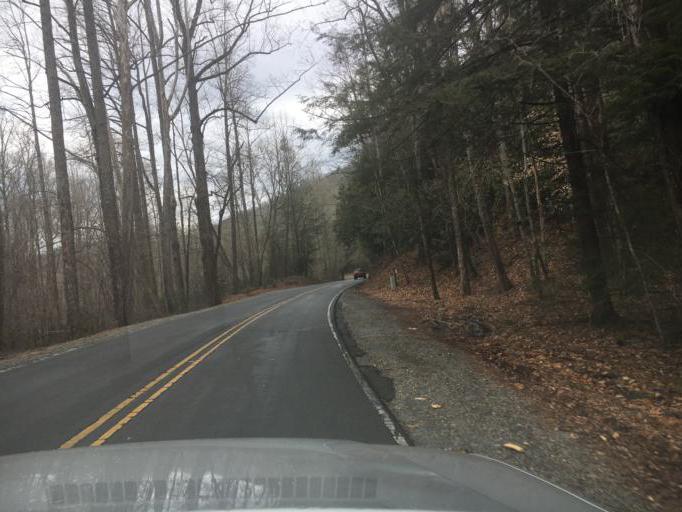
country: US
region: North Carolina
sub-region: Transylvania County
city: Brevard
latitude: 35.2769
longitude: -82.7126
